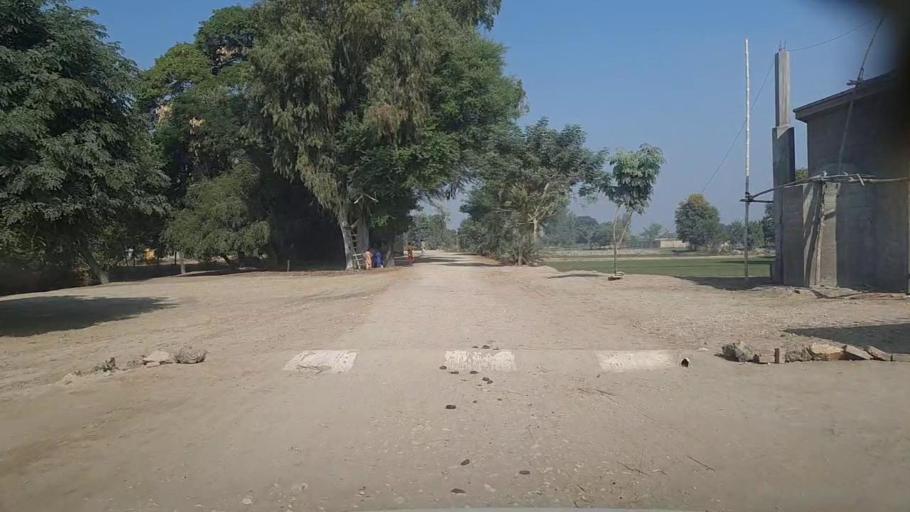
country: PK
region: Sindh
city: Kandiari
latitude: 26.9712
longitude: 68.4549
